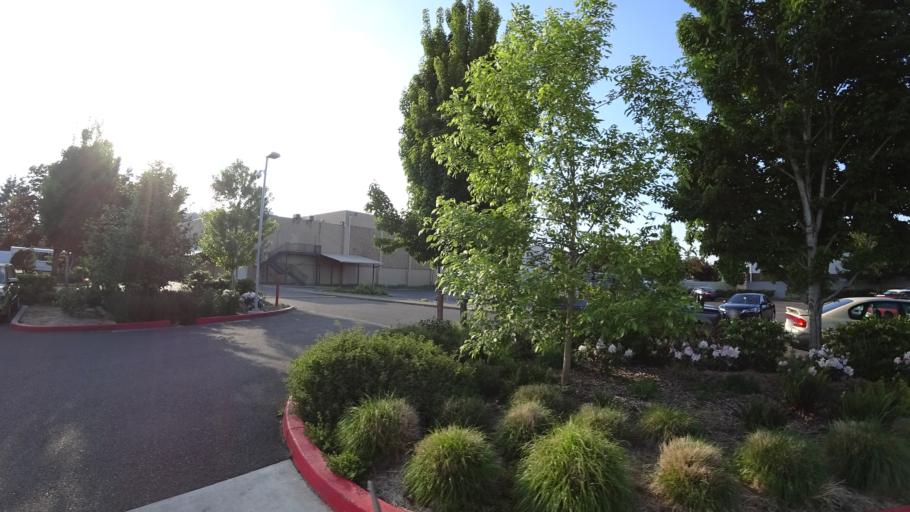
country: US
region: Oregon
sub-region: Multnomah County
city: Lents
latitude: 45.5081
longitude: -122.5795
